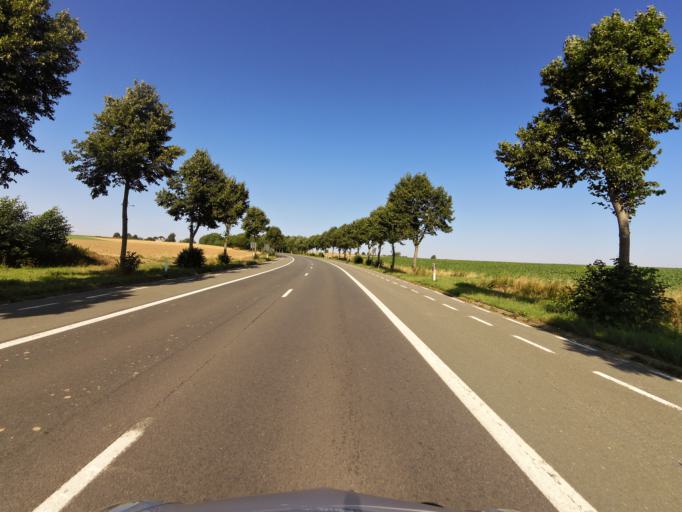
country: BE
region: Wallonia
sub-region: Province du Hainaut
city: Flobecq
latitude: 50.8194
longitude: 3.7129
